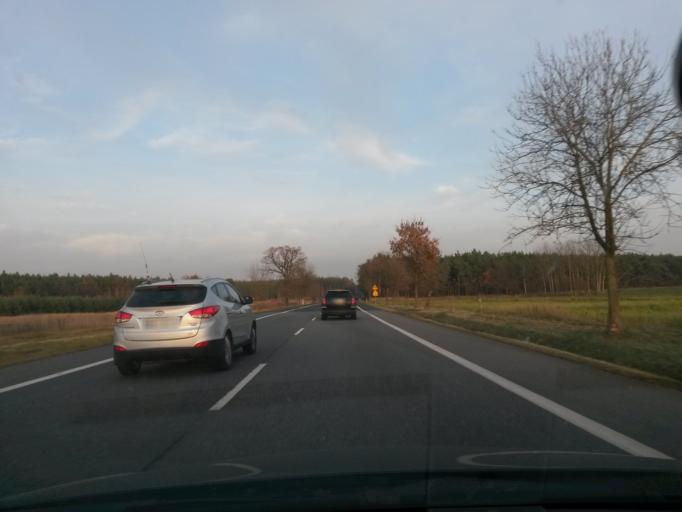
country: PL
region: Lodz Voivodeship
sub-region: Powiat wielunski
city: Wierzchlas
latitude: 51.2472
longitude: 18.6975
